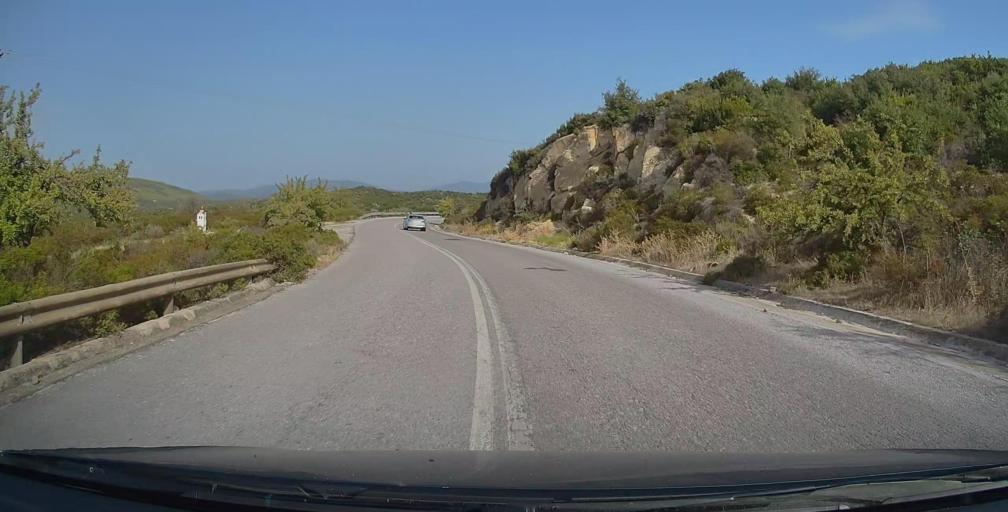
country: GR
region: Central Macedonia
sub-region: Nomos Chalkidikis
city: Sykia
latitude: 39.9768
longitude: 23.9592
